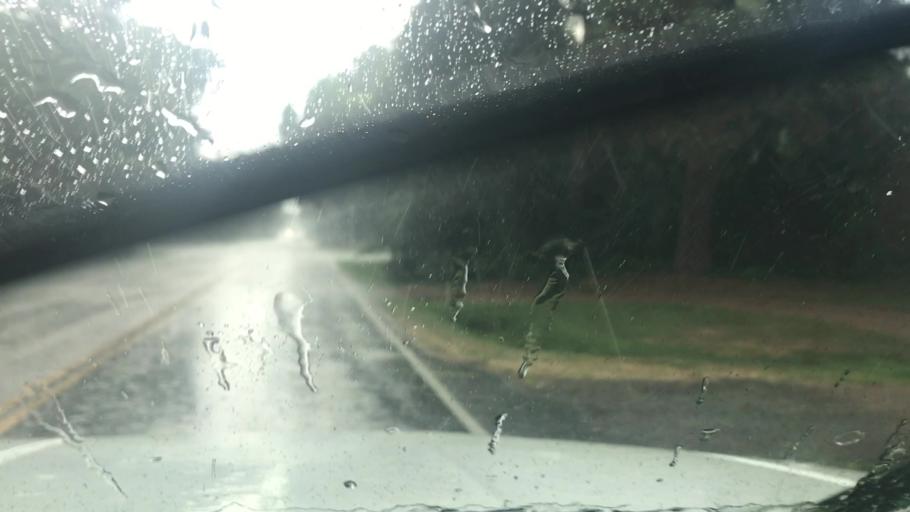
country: US
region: Virginia
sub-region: Henrico County
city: Tuckahoe
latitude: 37.5977
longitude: -77.5376
